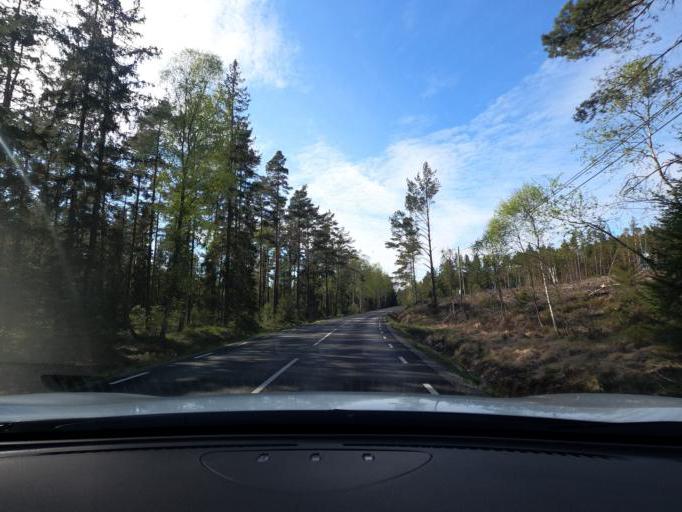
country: SE
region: Vaestra Goetaland
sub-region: Harryda Kommun
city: Landvetter
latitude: 57.6366
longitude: 12.2595
